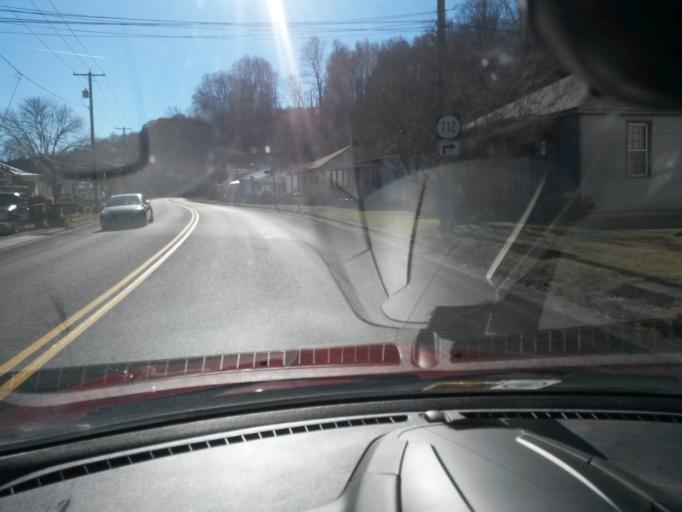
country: US
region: Virginia
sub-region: Henry County
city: Bassett
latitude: 36.7615
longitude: -79.9955
